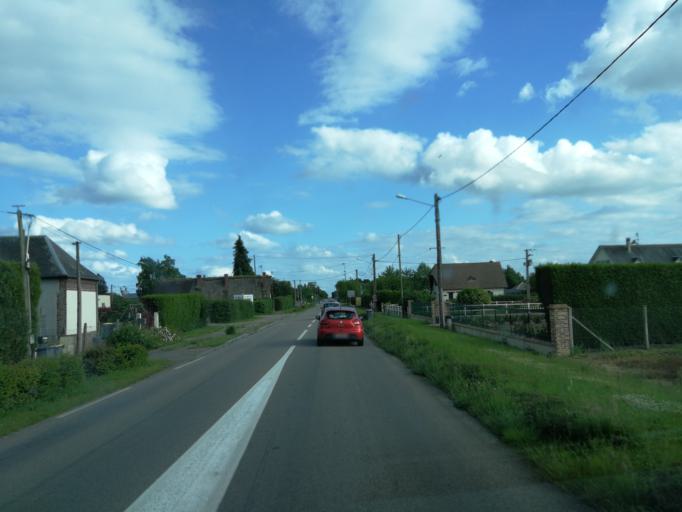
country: FR
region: Haute-Normandie
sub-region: Departement de l'Eure
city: Le Neubourg
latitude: 49.1224
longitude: 0.9098
